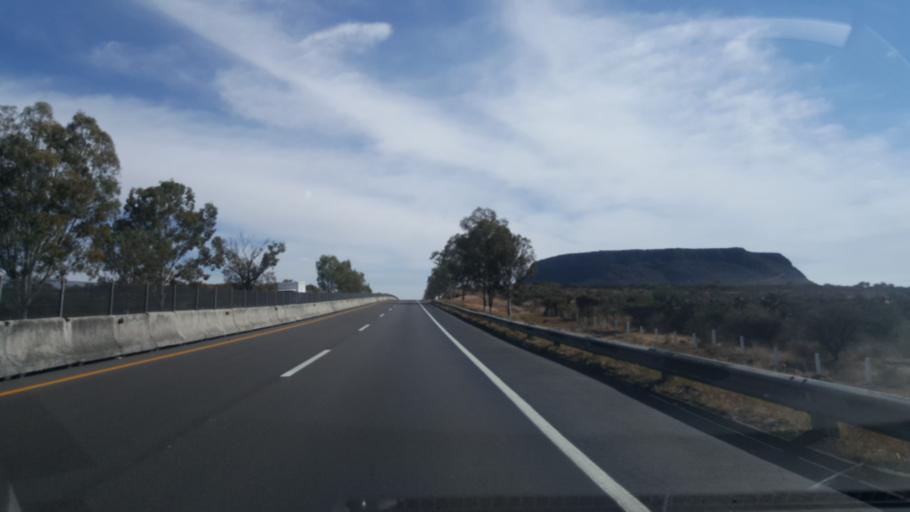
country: MX
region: Jalisco
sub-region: Lagos de Moreno
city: Cristeros [Fraccionamiento]
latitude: 21.3009
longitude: -102.0198
